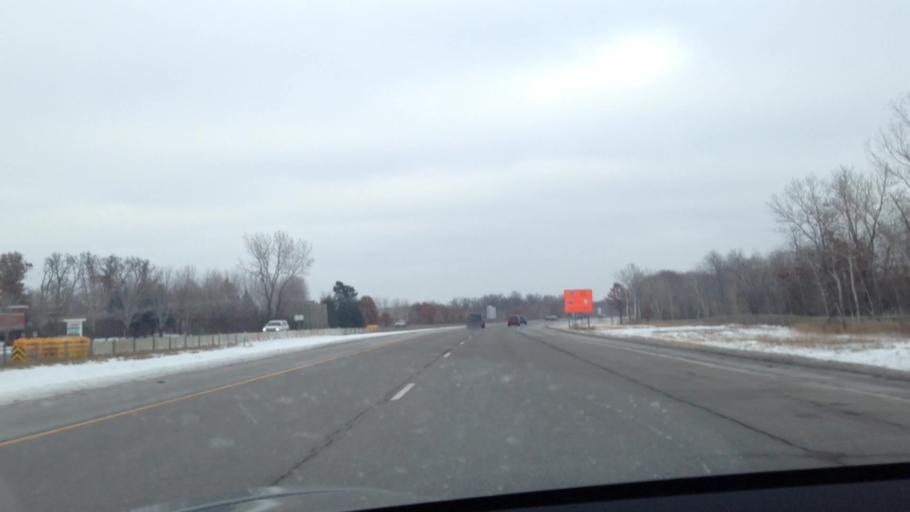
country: US
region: Minnesota
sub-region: Anoka County
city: Circle Pines
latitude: 45.1620
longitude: -93.1596
